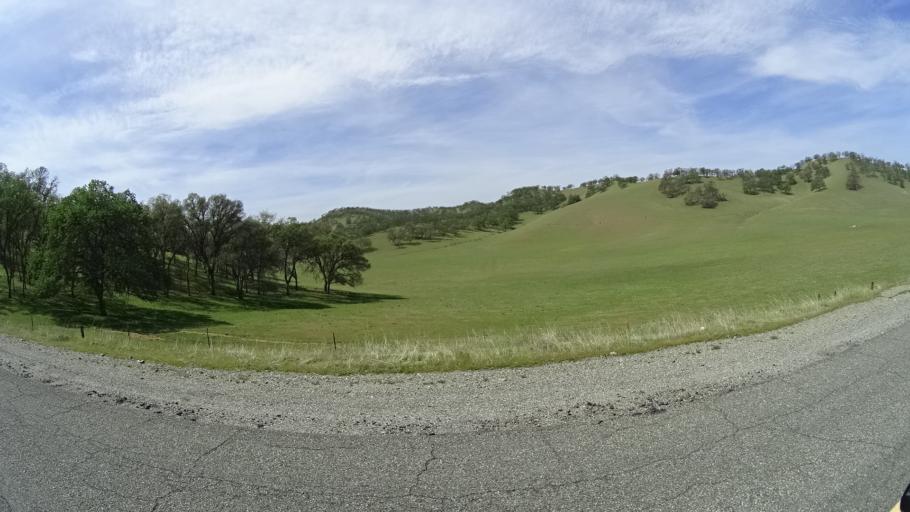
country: US
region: California
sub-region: Glenn County
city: Willows
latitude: 39.5740
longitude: -122.4445
